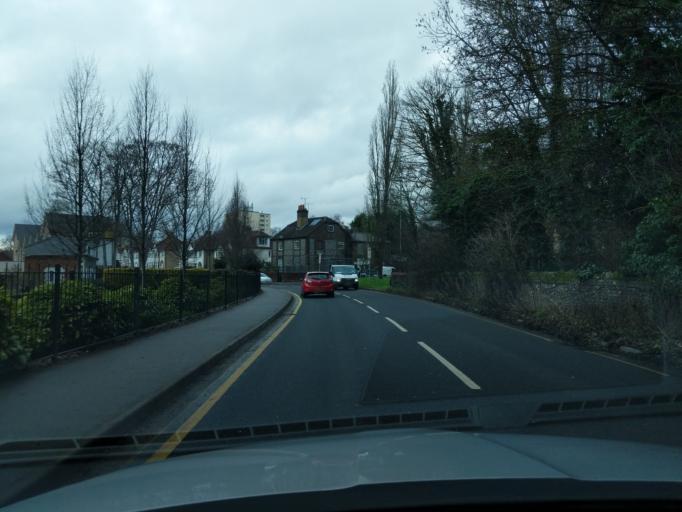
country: GB
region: England
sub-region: Hertfordshire
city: Kings Langley
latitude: 51.7295
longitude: -0.4505
